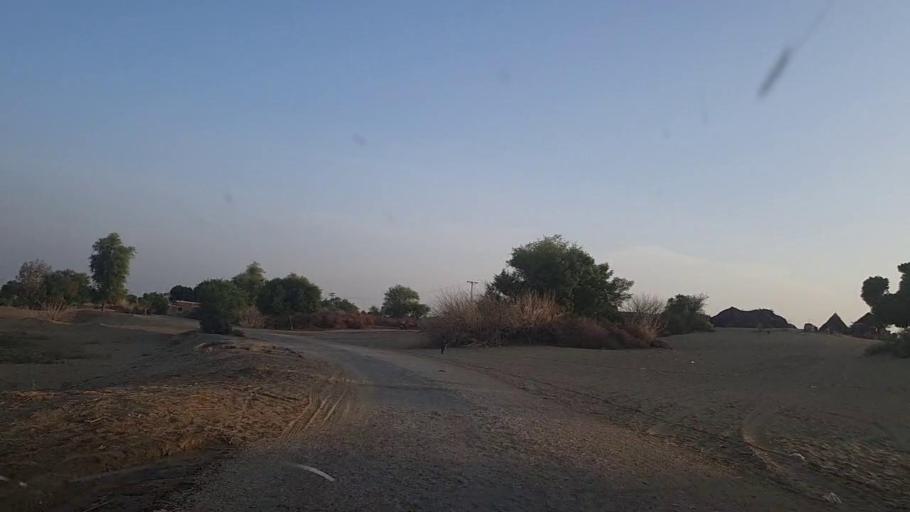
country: PK
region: Sindh
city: Khanpur
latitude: 27.6256
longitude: 69.4444
